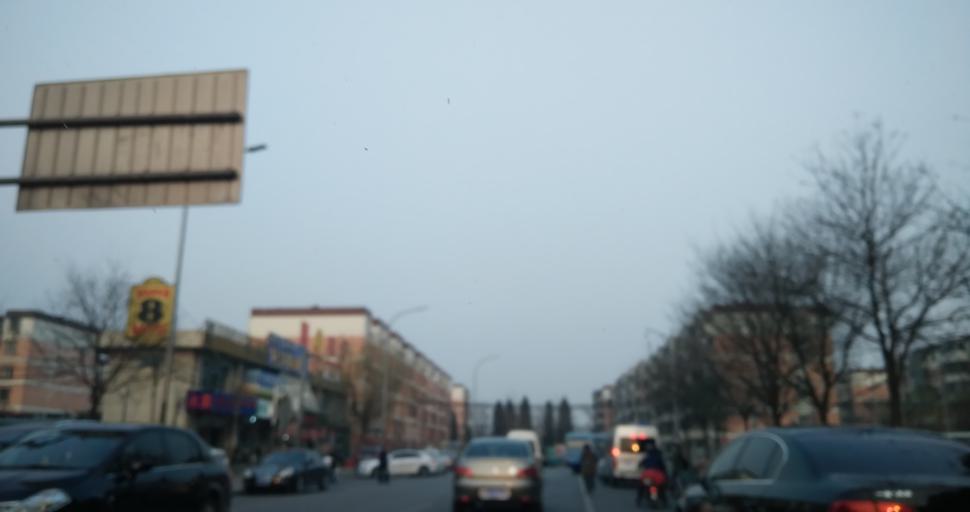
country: CN
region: Beijing
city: Xingfeng
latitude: 39.7306
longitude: 116.3416
